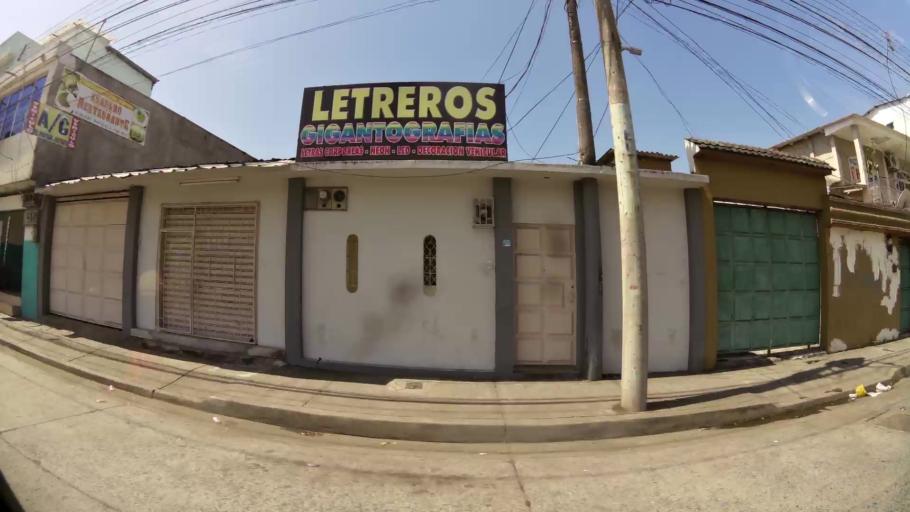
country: EC
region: Guayas
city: Eloy Alfaro
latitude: -2.1196
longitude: -79.9055
